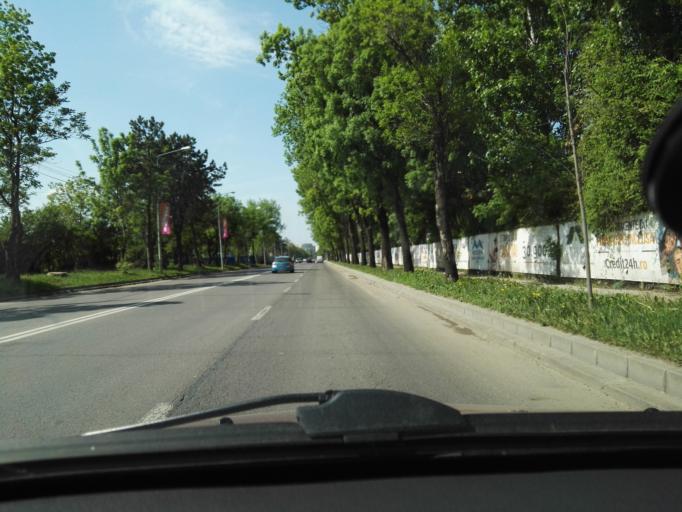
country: RO
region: Ilfov
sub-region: Comuna Popesti-Leordeni
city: Popesti-Leordeni
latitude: 44.3686
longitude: 26.1243
